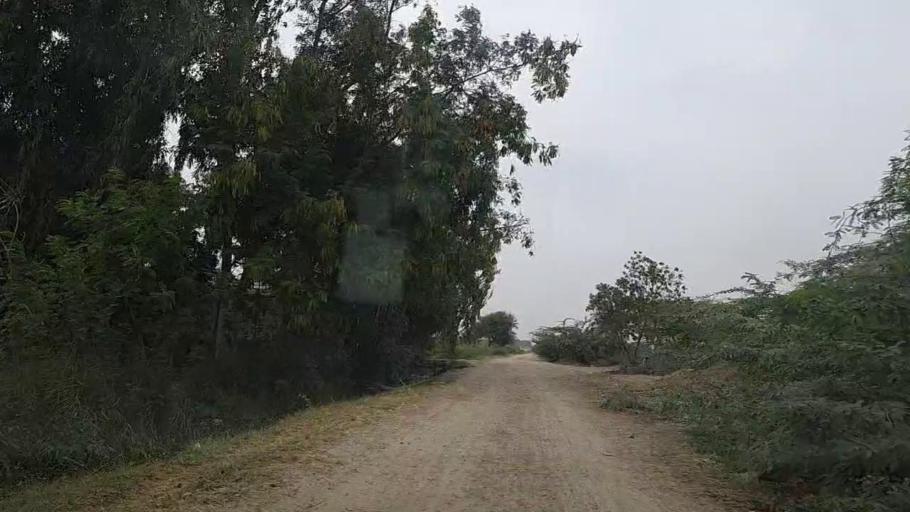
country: PK
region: Sindh
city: Mirpur Sakro
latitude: 24.6138
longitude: 67.7178
